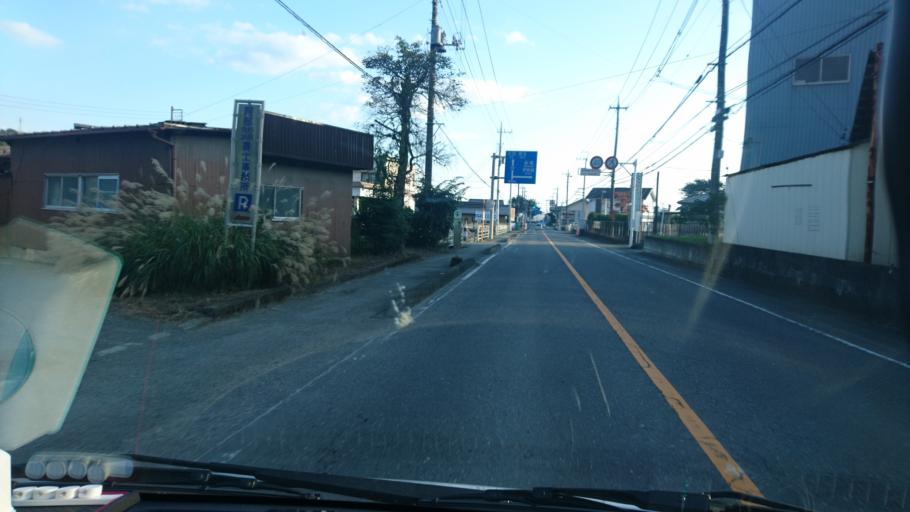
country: JP
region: Gunma
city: Omamacho-omama
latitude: 36.4492
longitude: 139.2747
